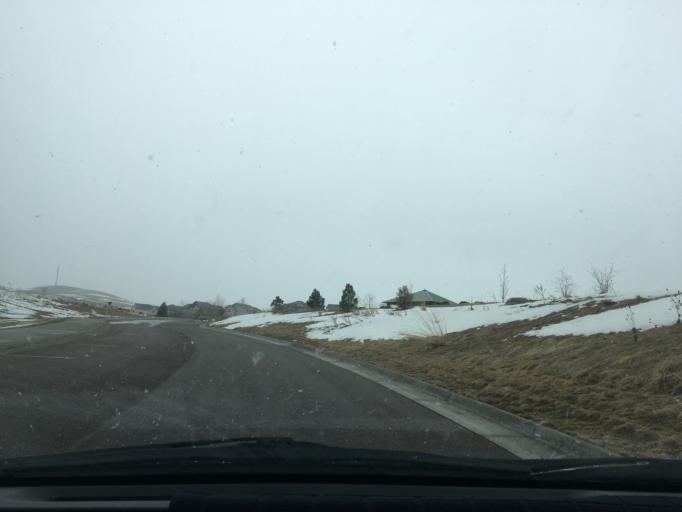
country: US
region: Colorado
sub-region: Boulder County
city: Superior
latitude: 39.9235
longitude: -105.1603
